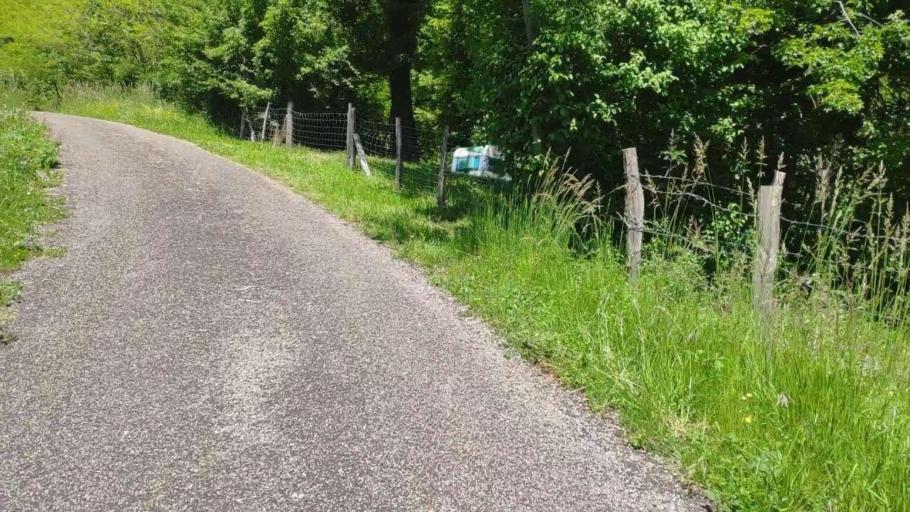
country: FR
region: Franche-Comte
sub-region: Departement du Jura
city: Poligny
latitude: 46.7625
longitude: 5.6812
